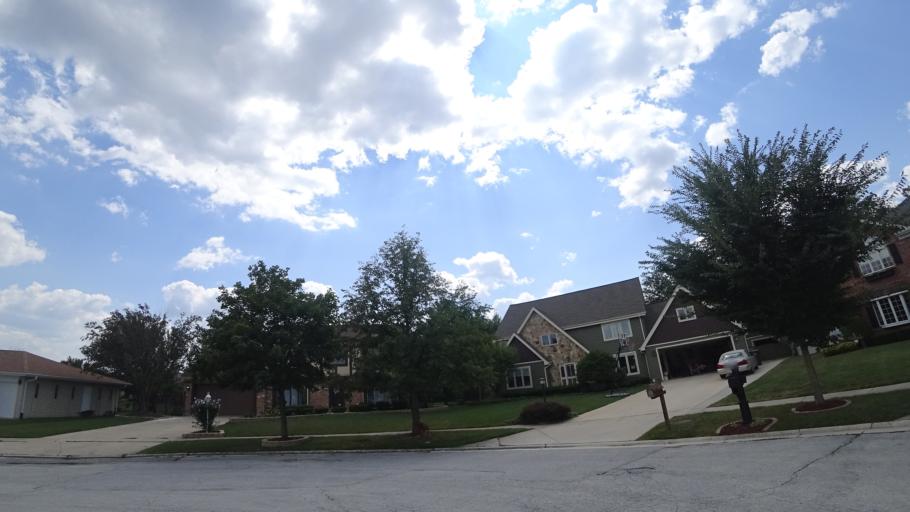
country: US
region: Illinois
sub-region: Cook County
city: Oak Forest
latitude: 41.6196
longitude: -87.7756
